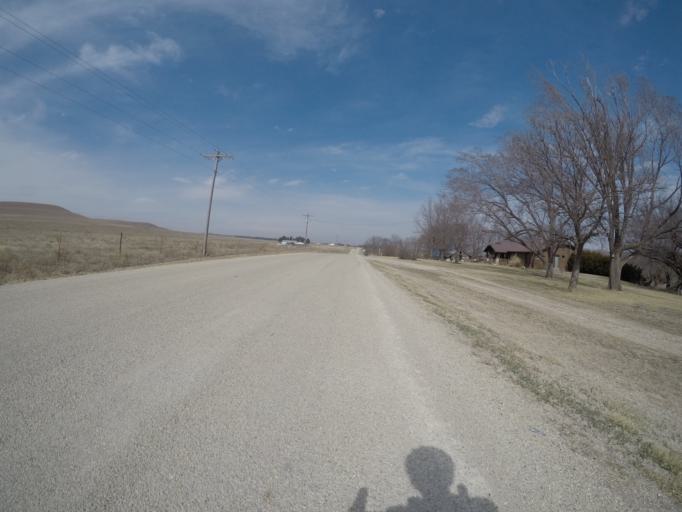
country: US
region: Kansas
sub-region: Geary County
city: Grandview Plaza
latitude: 39.0300
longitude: -96.7430
